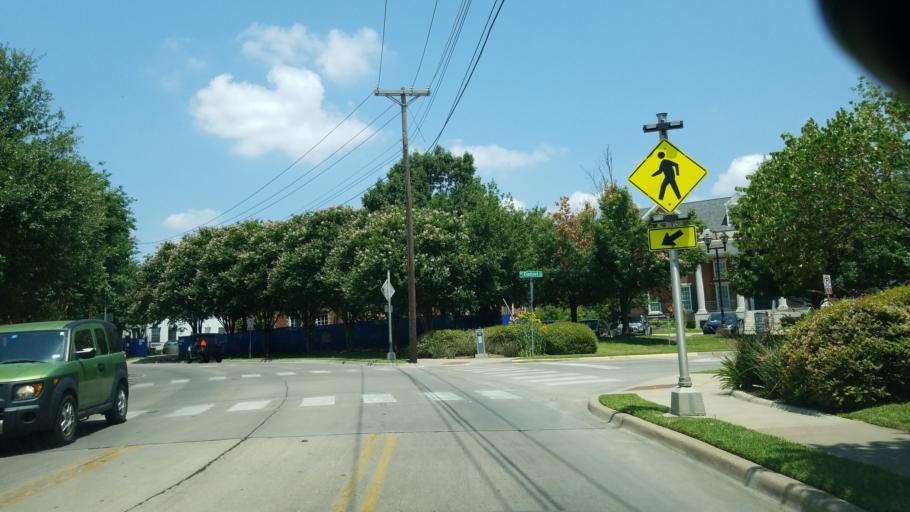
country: US
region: Texas
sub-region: Dallas County
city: Highland Park
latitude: 32.8464
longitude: -96.7818
